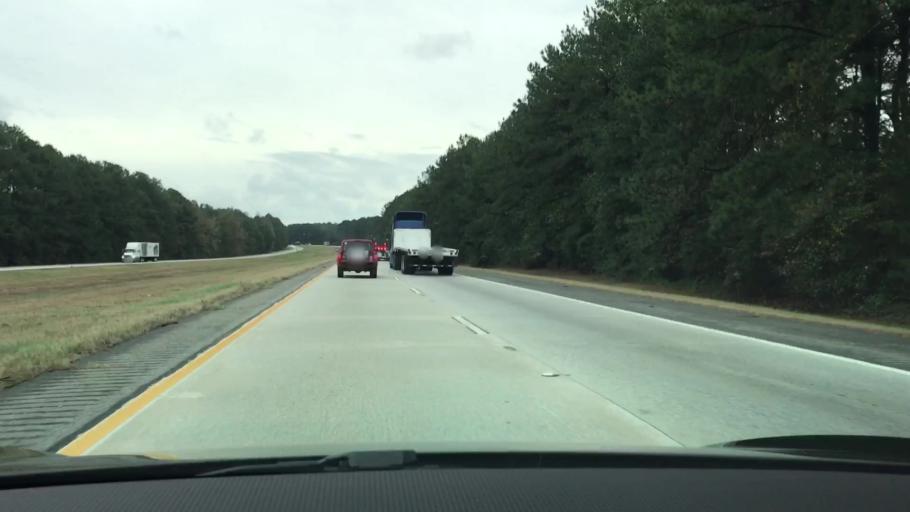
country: US
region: Georgia
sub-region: Taliaferro County
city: Crawfordville
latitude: 33.5362
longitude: -82.9958
